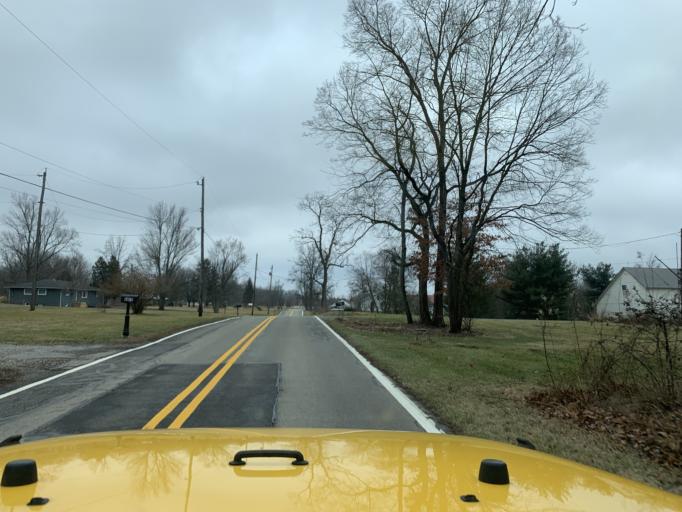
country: US
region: Ohio
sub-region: Franklin County
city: New Albany
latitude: 40.0957
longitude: -82.7931
